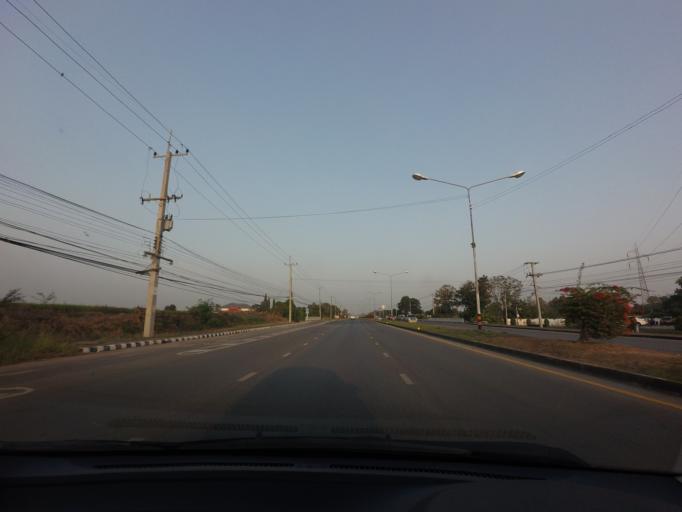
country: TH
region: Sukhothai
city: Sukhothai
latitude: 17.0207
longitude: 99.8637
